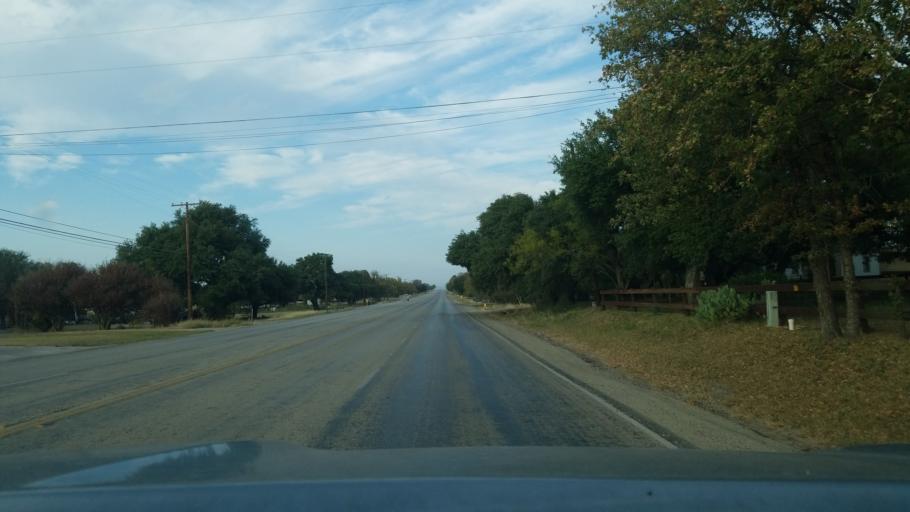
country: US
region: Texas
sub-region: Brown County
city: Early
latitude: 31.7588
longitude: -98.9586
